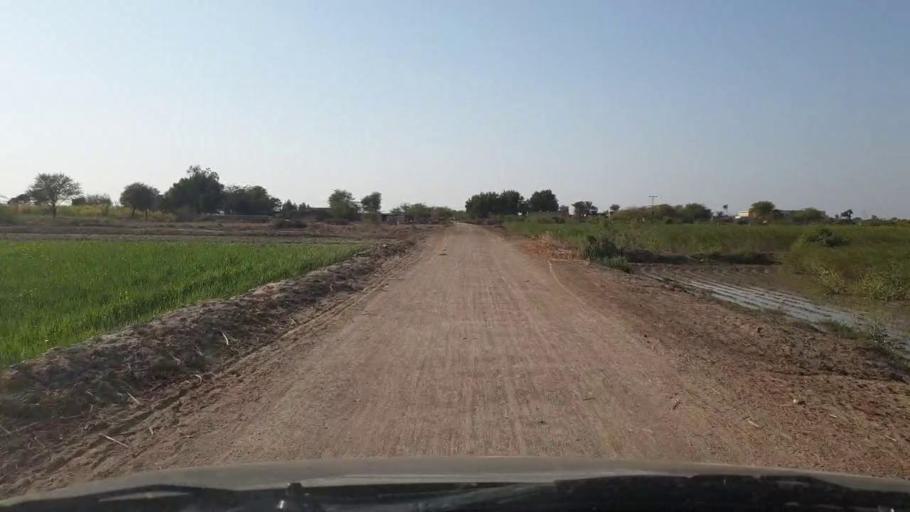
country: PK
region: Sindh
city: Digri
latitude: 25.1460
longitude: 69.2839
